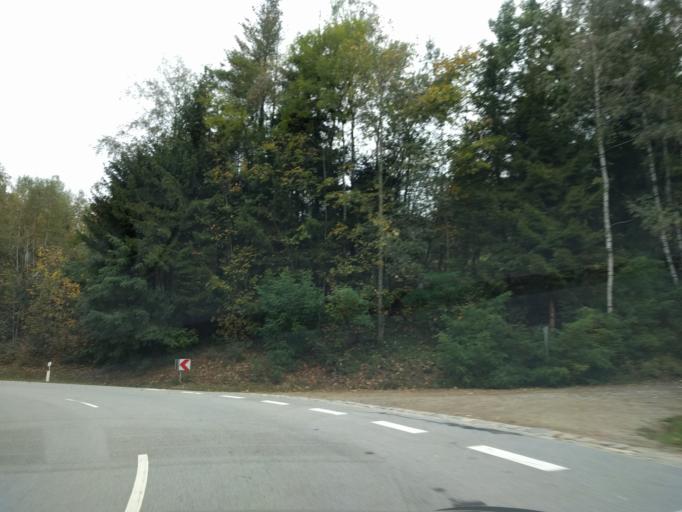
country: DE
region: Bavaria
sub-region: Lower Bavaria
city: Schaufling
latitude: 48.8747
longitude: 13.0892
